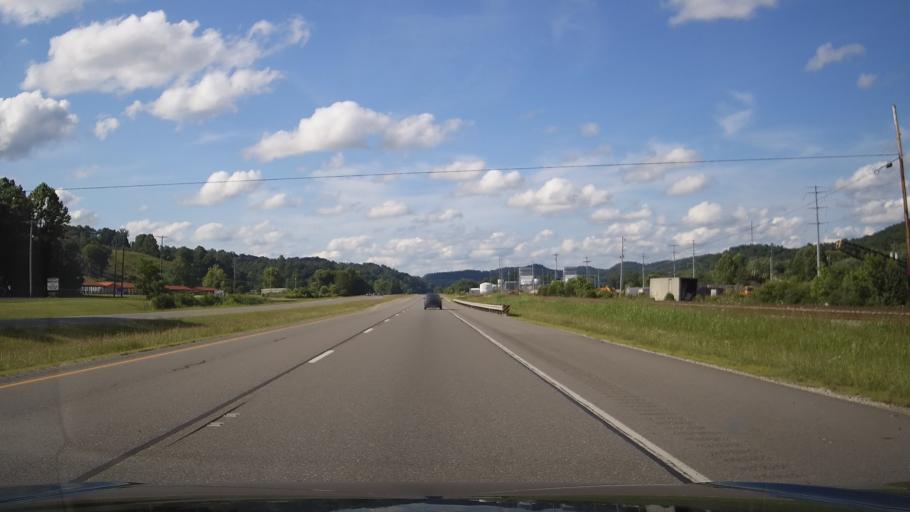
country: US
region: Kentucky
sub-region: Lawrence County
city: Louisa
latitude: 38.1836
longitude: -82.6078
